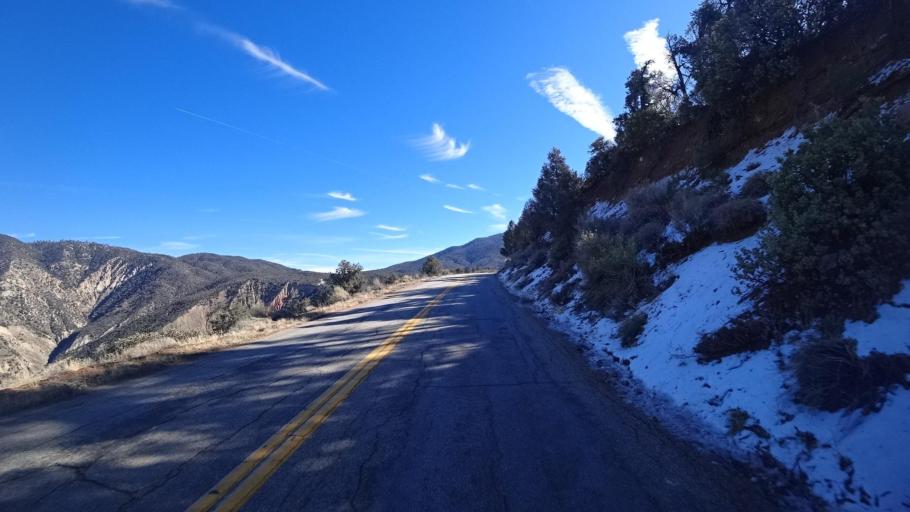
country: US
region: California
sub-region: Kern County
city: Pine Mountain Club
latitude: 34.8670
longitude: -119.2547
